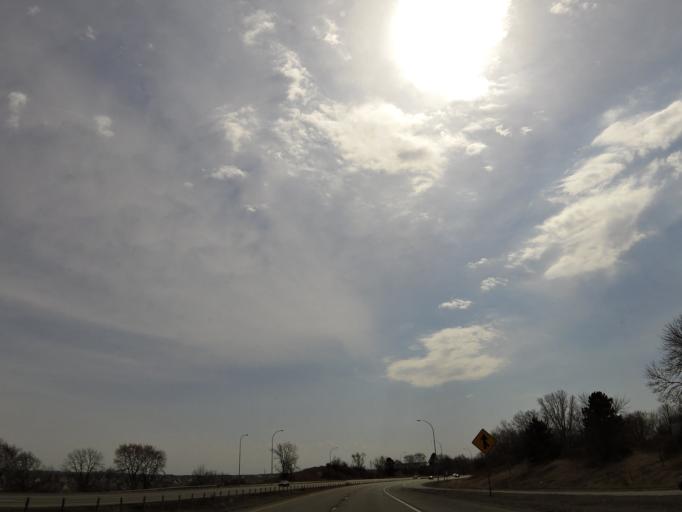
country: US
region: Minnesota
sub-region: Dakota County
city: South Saint Paul
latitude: 44.8840
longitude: -93.0627
